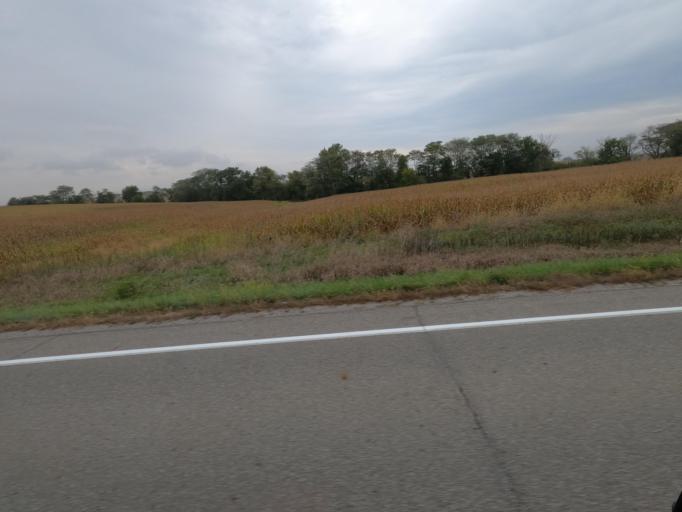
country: US
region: Iowa
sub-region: Van Buren County
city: Keosauqua
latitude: 40.8134
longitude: -91.8062
